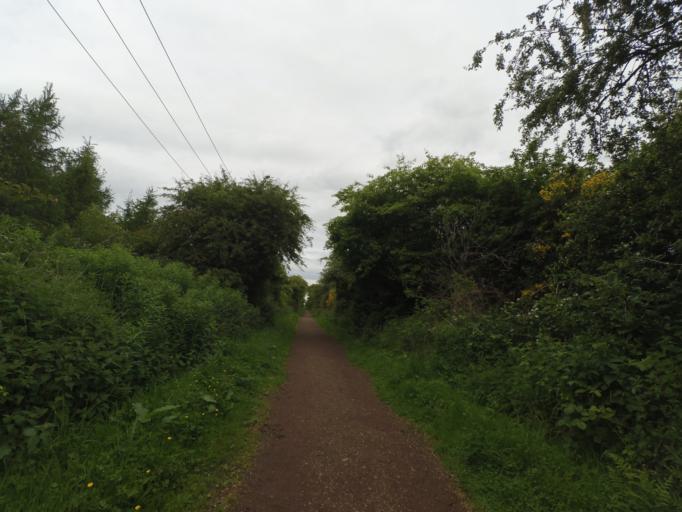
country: GB
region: Scotland
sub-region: East Lothian
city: Macmerry
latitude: 55.9318
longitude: -2.9111
